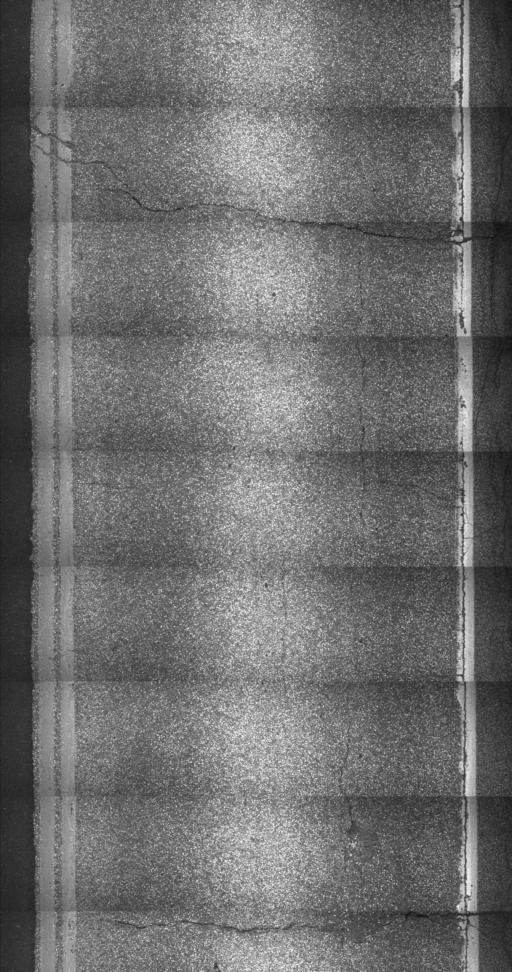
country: US
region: New Hampshire
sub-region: Grafton County
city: Woodsville
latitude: 44.2170
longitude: -72.2115
